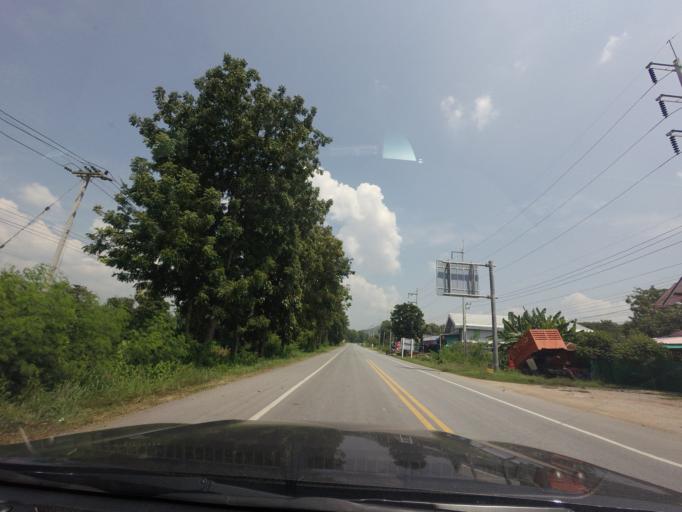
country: TH
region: Uttaradit
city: Thong Saen Khan
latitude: 17.4725
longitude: 100.2381
